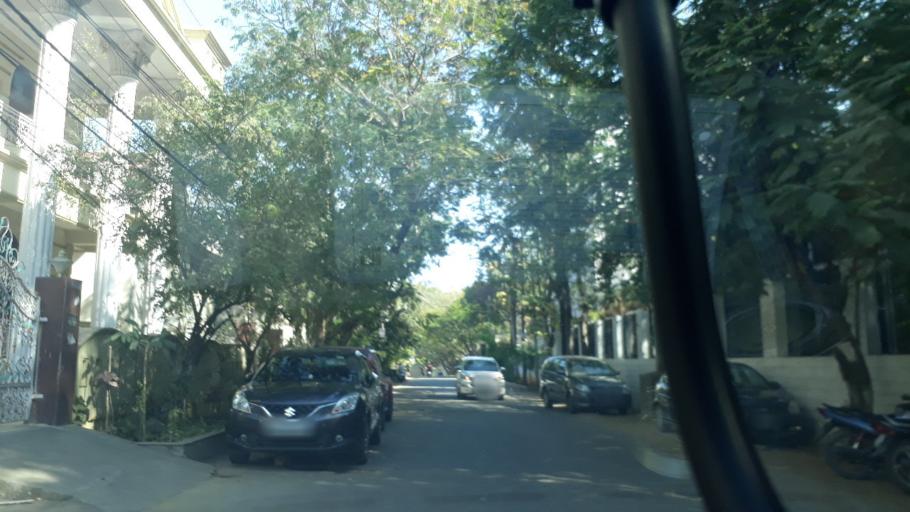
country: IN
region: Telangana
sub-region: Rangareddi
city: Kukatpalli
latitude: 17.4221
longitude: 78.4007
